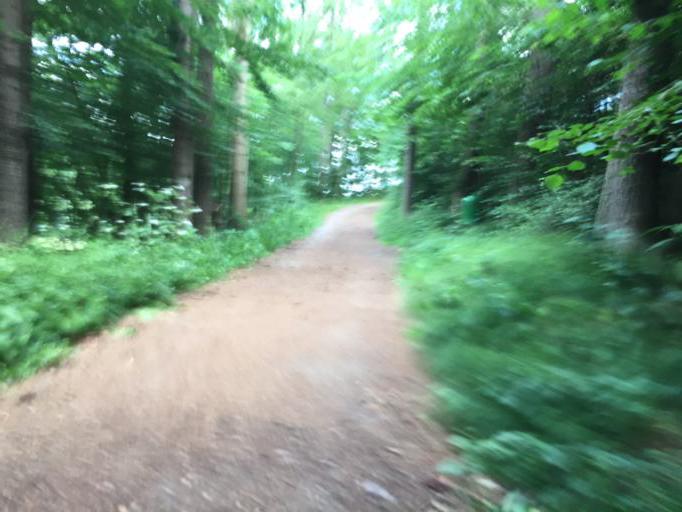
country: DE
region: Rheinland-Pfalz
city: Holler
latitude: 50.4257
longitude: 7.8508
